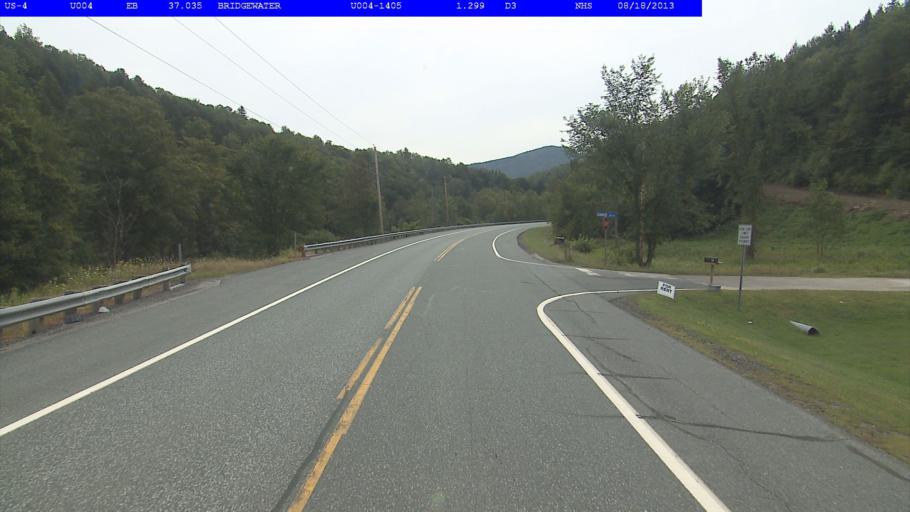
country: US
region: Vermont
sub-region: Windsor County
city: Woodstock
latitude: 43.6023
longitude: -72.7261
